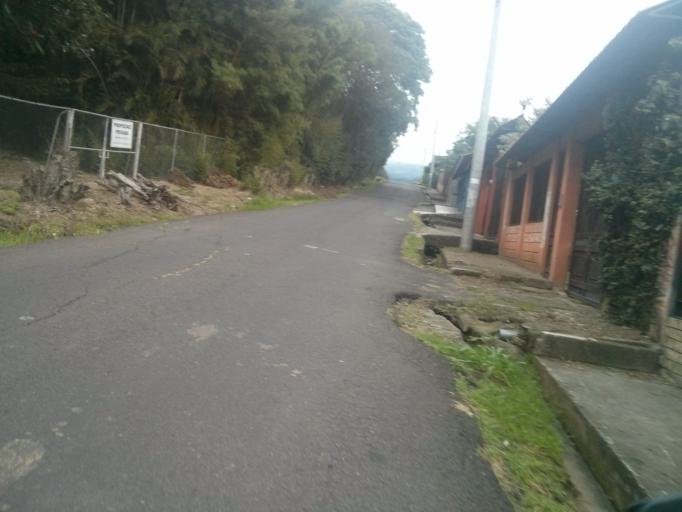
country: CR
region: Heredia
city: Angeles
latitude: 10.0189
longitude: -84.0486
